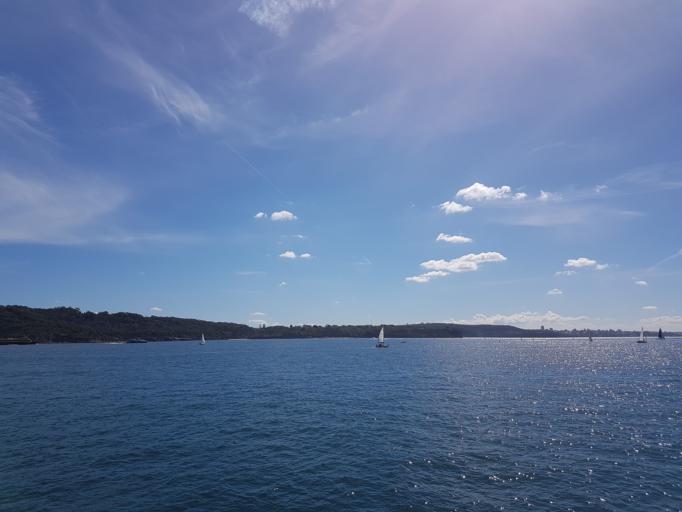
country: AU
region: New South Wales
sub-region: Waverley
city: Dover Heights
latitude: -33.8448
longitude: 151.2706
